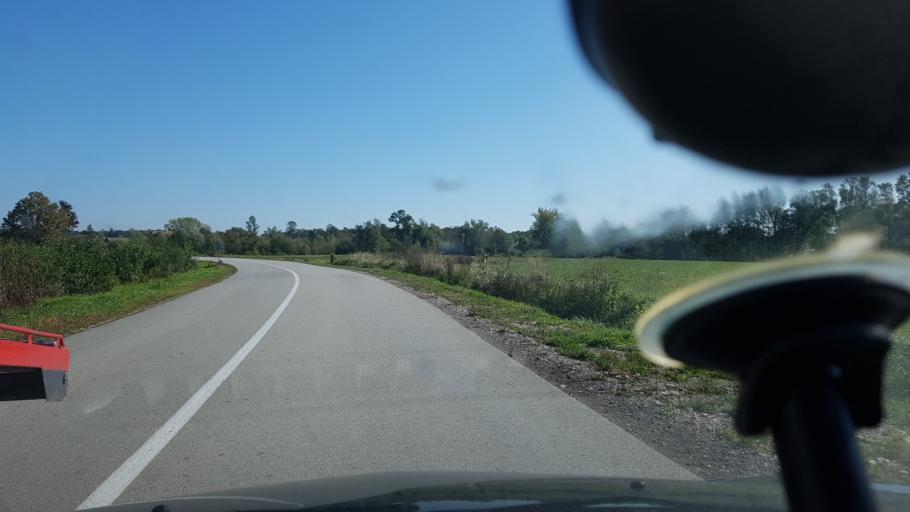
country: HR
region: Zagrebacka
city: Brckovljani
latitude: 45.7596
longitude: 16.2601
